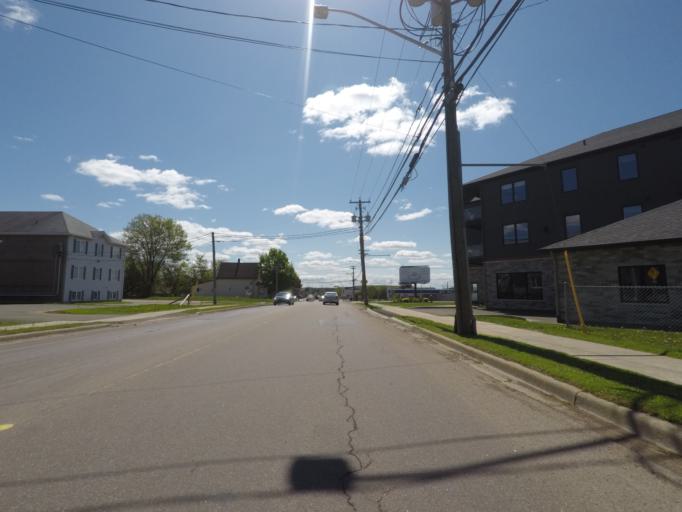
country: CA
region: New Brunswick
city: Moncton
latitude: 46.0960
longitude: -64.7524
